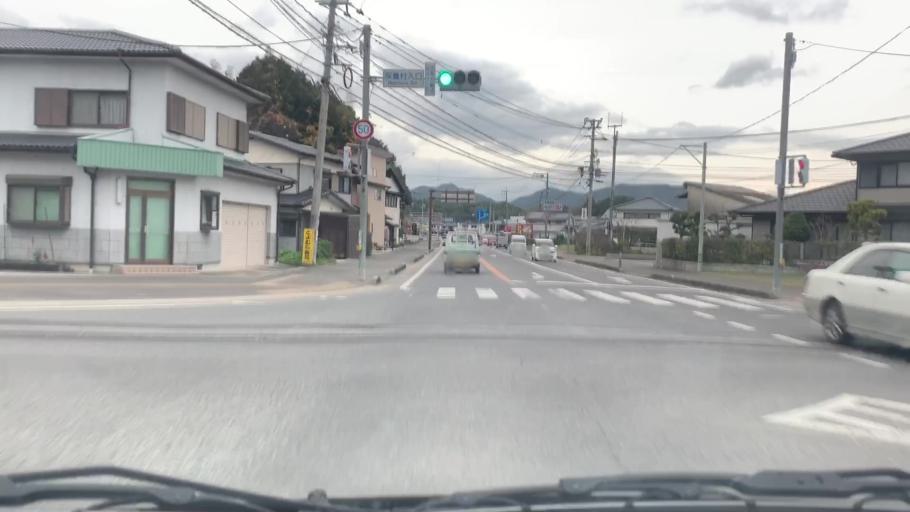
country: JP
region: Saga Prefecture
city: Takeocho-takeo
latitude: 33.1839
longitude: 130.0395
